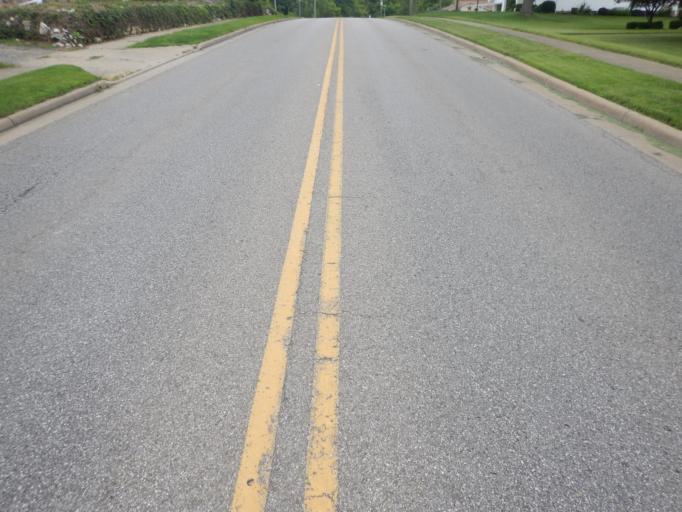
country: US
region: Ohio
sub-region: Muskingum County
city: North Zanesville
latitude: 39.9641
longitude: -82.0166
